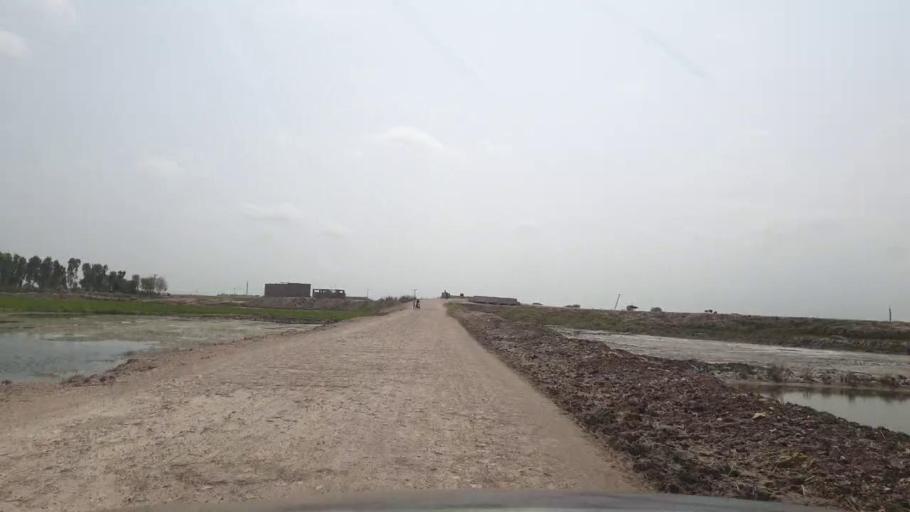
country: PK
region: Sindh
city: Ratodero
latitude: 27.8391
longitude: 68.3340
